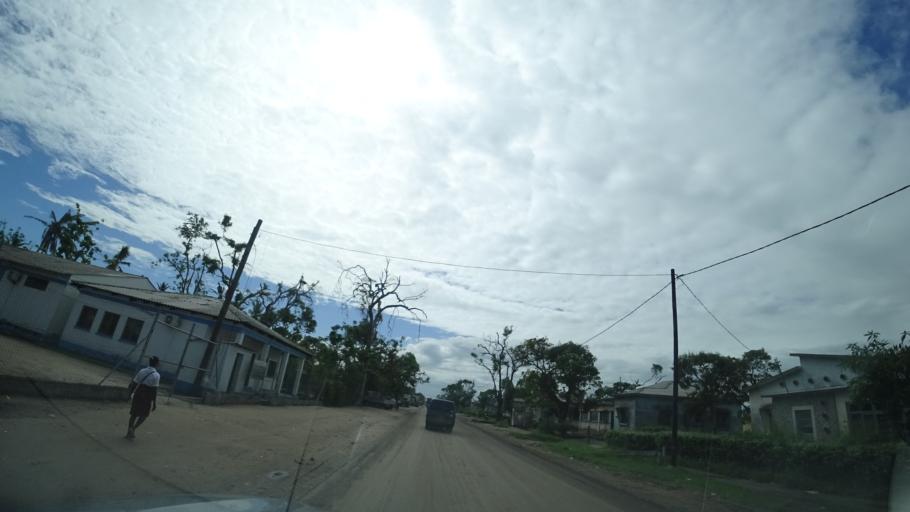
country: MZ
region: Sofala
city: Beira
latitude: -19.7701
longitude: 34.8687
